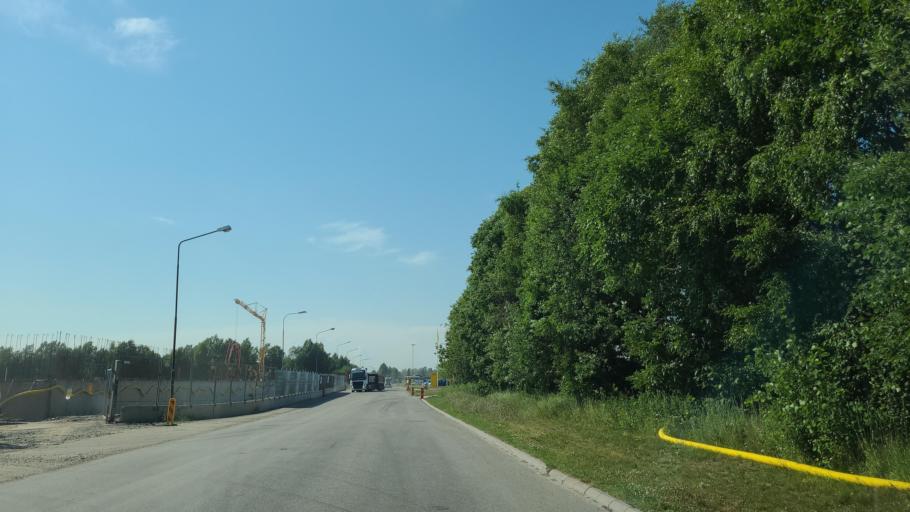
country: SE
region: Vaesterbotten
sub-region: Umea Kommun
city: Umea
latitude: 63.8426
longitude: 20.2220
